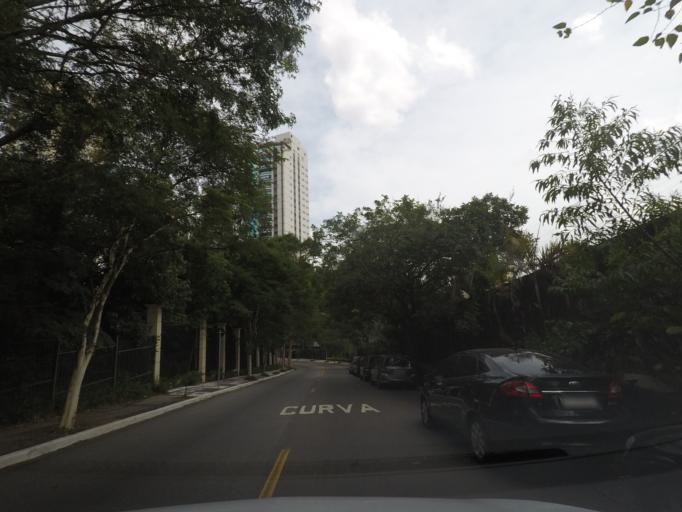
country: BR
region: Sao Paulo
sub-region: Taboao Da Serra
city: Taboao da Serra
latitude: -23.6315
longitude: -46.7243
